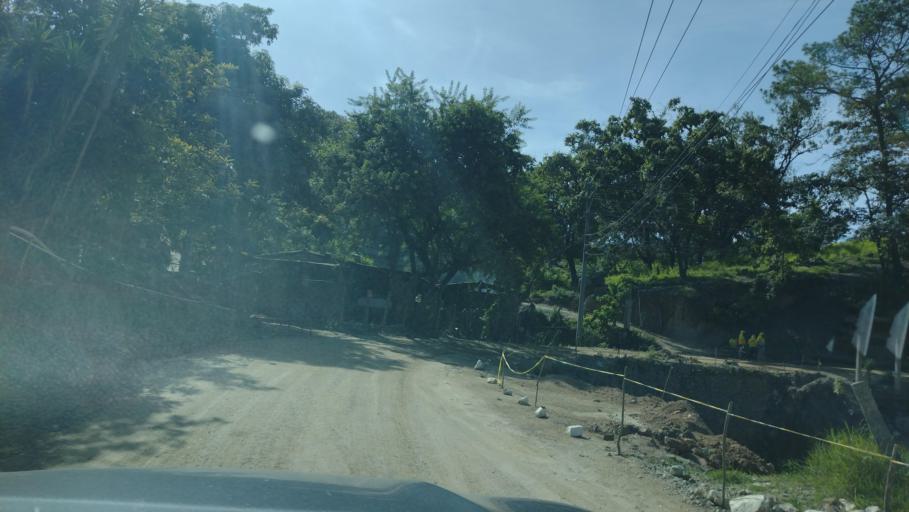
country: GT
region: Guatemala
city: Chinautla
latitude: 14.7628
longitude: -90.5257
